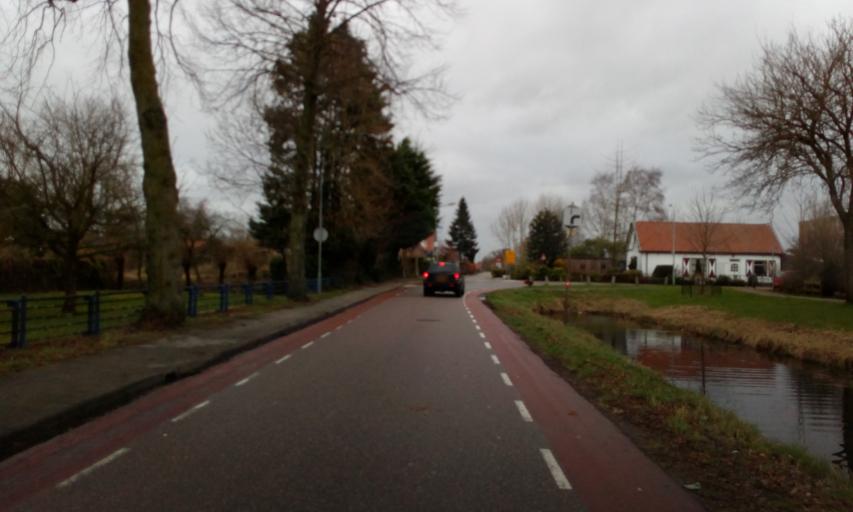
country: NL
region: North Holland
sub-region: Gemeente Wijdemeren
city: Kortenhoef
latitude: 52.2413
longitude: 5.1090
